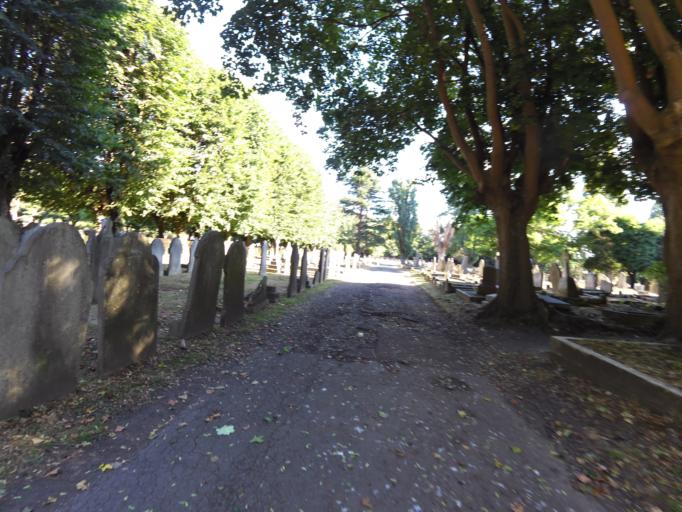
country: GB
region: England
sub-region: Greater London
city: Harringay
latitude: 51.6022
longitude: -0.0778
